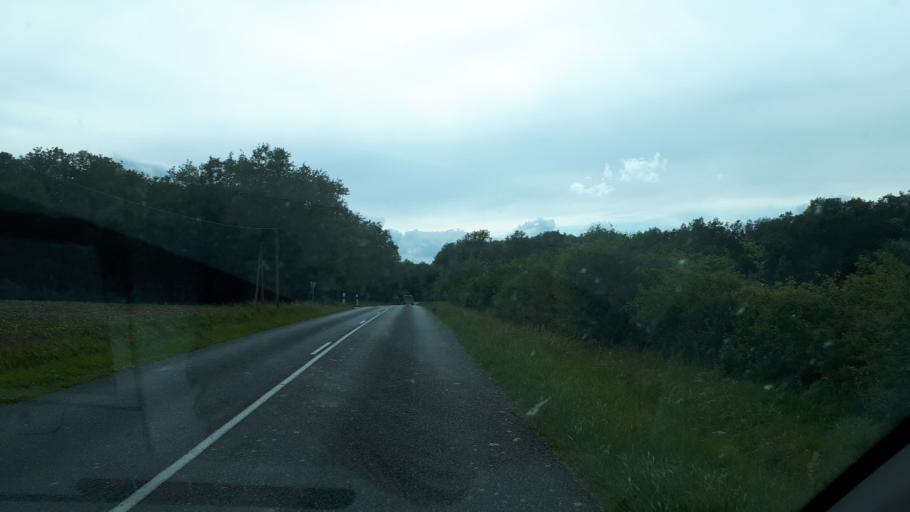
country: FR
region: Centre
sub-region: Departement du Cher
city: Marmagne
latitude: 47.0790
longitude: 2.2964
